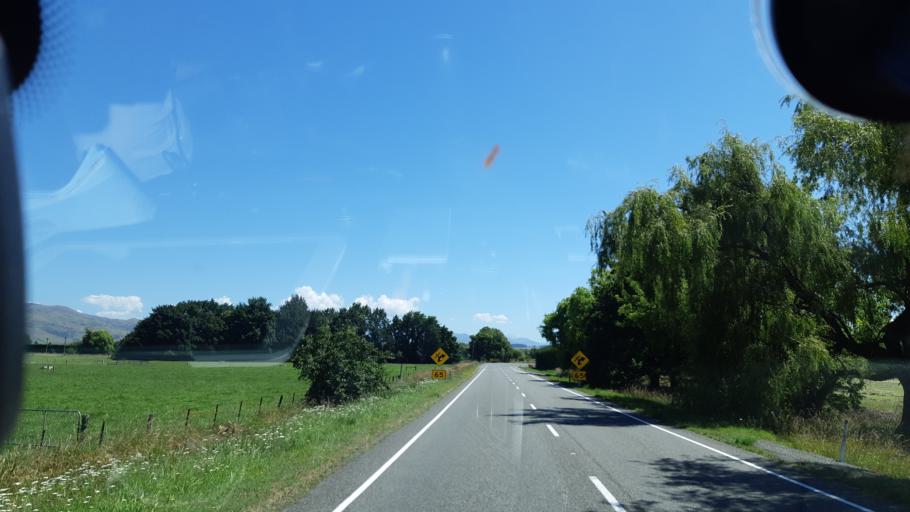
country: NZ
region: Canterbury
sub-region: Kaikoura District
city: Kaikoura
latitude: -42.7421
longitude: 173.2668
